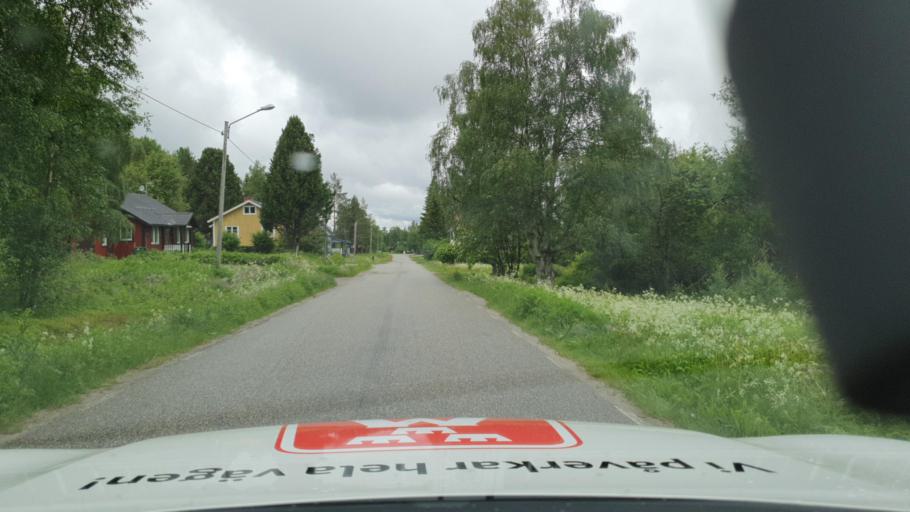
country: SE
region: Vaesterbotten
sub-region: Dorotea Kommun
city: Dorotea
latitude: 64.0995
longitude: 16.6455
